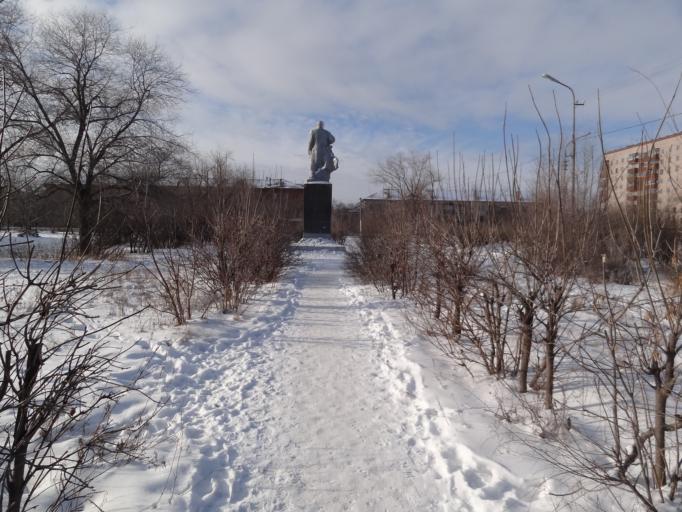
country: RU
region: Saratov
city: Engel's
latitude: 51.4811
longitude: 46.1585
